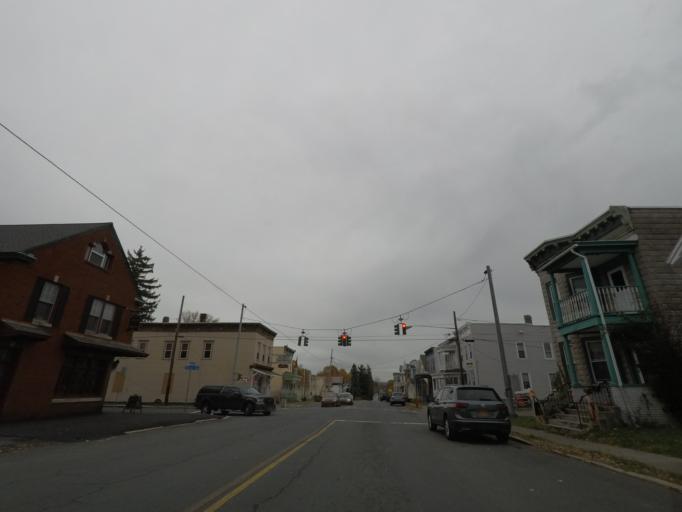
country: US
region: New York
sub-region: Albany County
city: Cohoes
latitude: 42.7721
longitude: -73.7128
